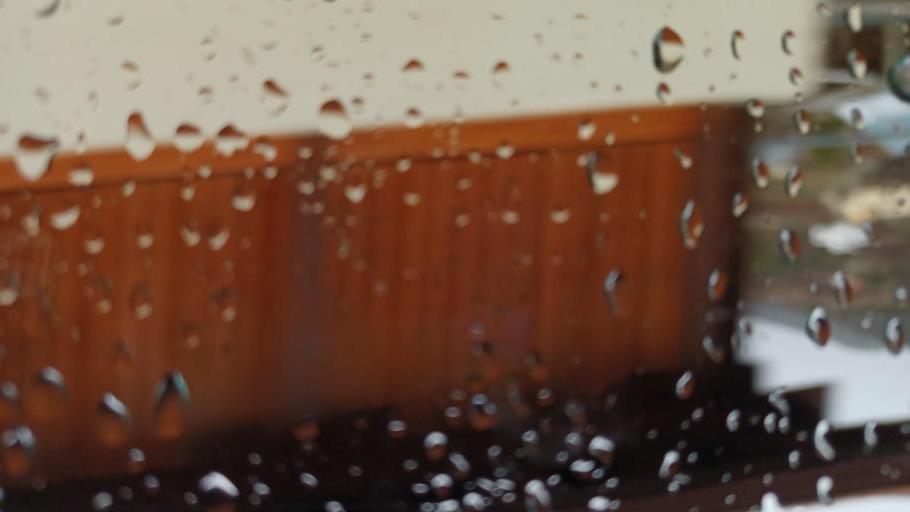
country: CY
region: Limassol
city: Kyperounta
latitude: 34.9436
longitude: 32.9787
